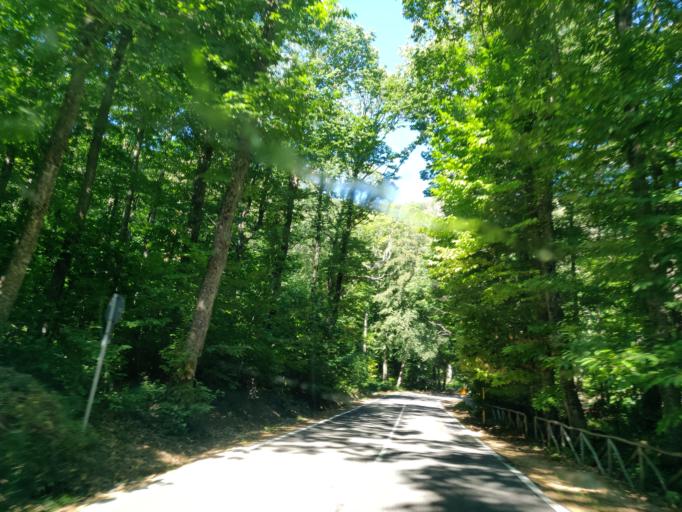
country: IT
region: Tuscany
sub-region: Provincia di Siena
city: Abbadia San Salvatore
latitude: 42.8967
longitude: 11.6499
